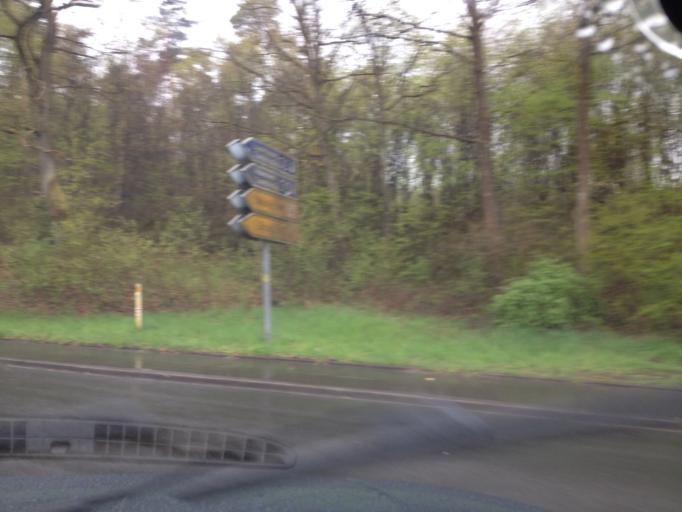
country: DE
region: Saarland
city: Bexbach
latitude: 49.3368
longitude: 7.2260
